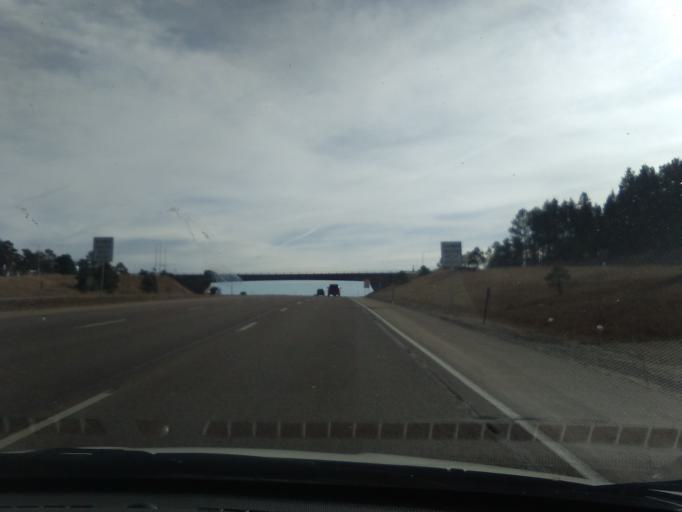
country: US
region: Colorado
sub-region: Jefferson County
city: Genesee
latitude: 39.7106
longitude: -105.2972
